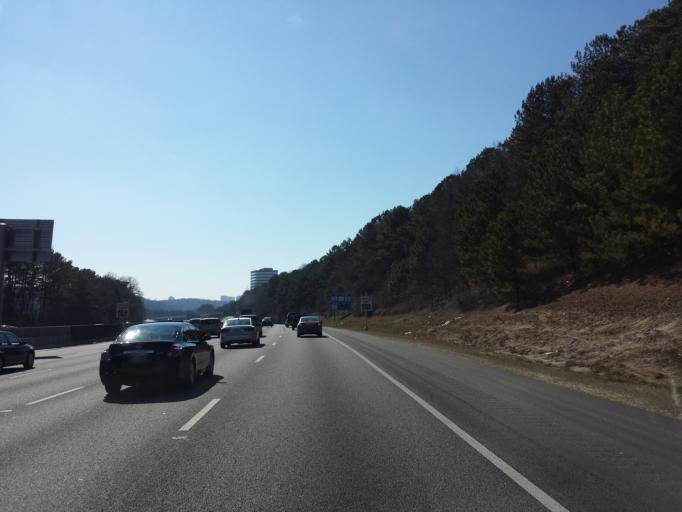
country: US
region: Georgia
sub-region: Fulton County
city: Sandy Springs
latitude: 33.9138
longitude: -84.4234
